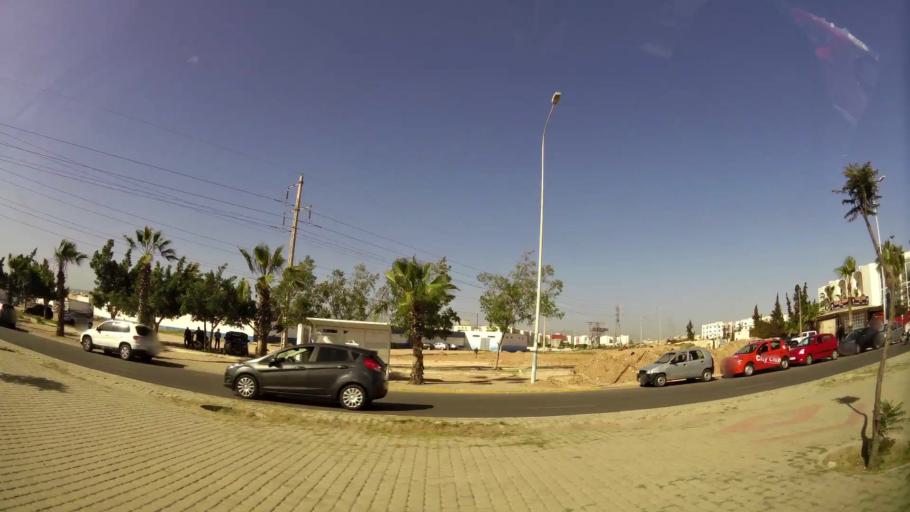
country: MA
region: Oued ed Dahab-Lagouira
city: Dakhla
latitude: 30.4137
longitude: -9.5676
